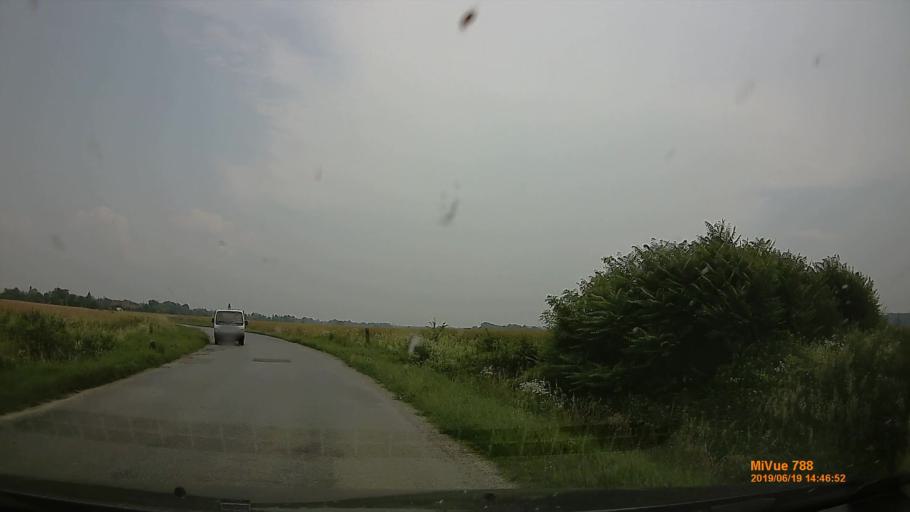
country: HU
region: Baranya
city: Szigetvar
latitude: 46.0011
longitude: 17.8258
